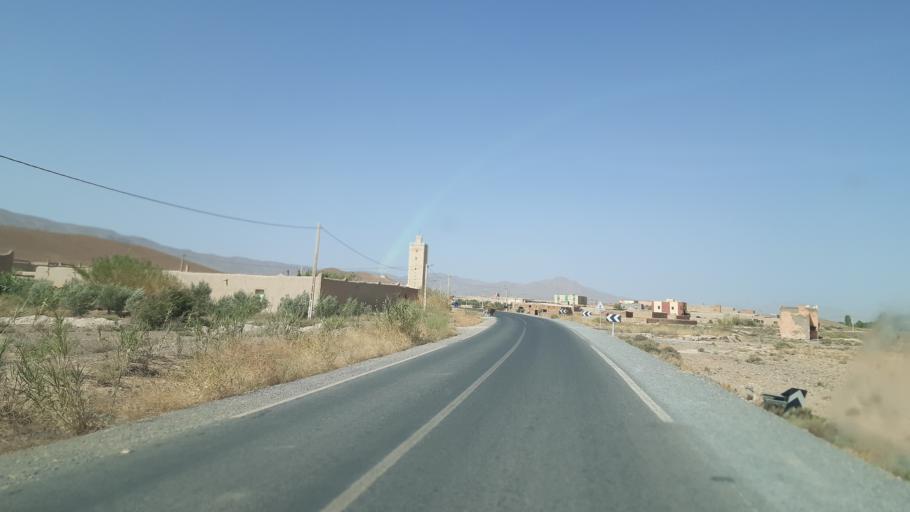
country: MA
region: Meknes-Tafilalet
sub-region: Errachidia
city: Errachidia
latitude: 32.2510
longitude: -4.5789
